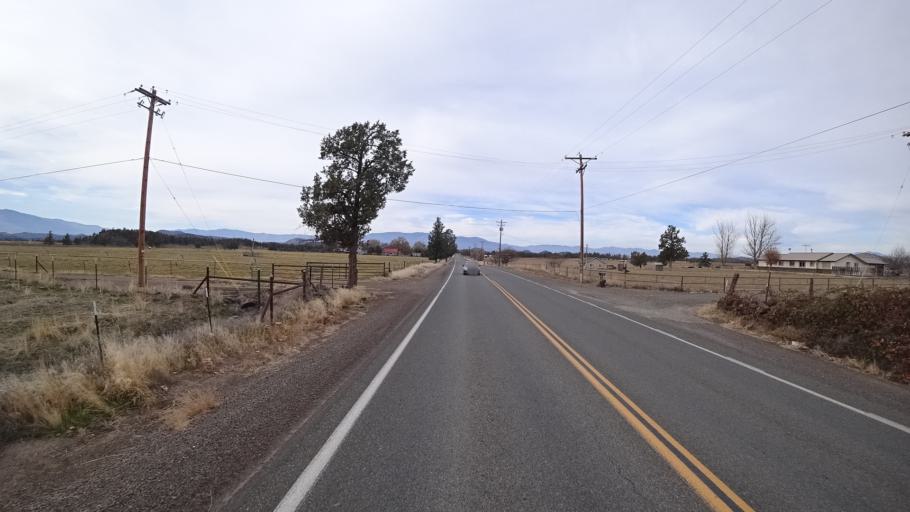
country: US
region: California
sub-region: Siskiyou County
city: Montague
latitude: 41.6241
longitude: -122.4092
